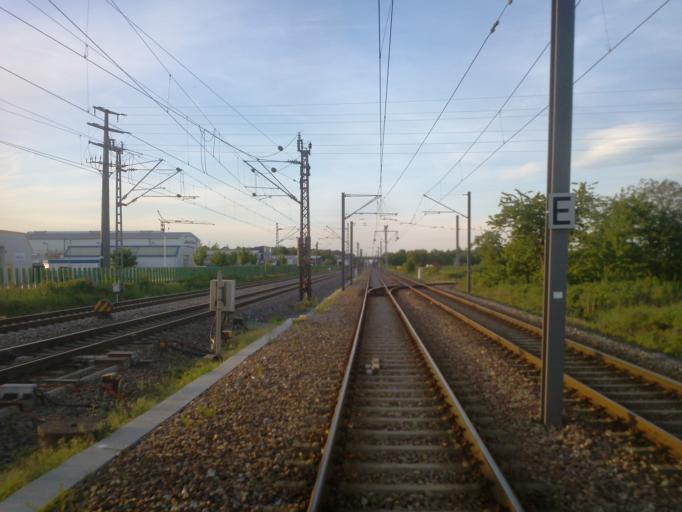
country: DE
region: Baden-Wuerttemberg
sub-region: Karlsruhe Region
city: Weingarten
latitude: 49.0744
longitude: 8.4672
